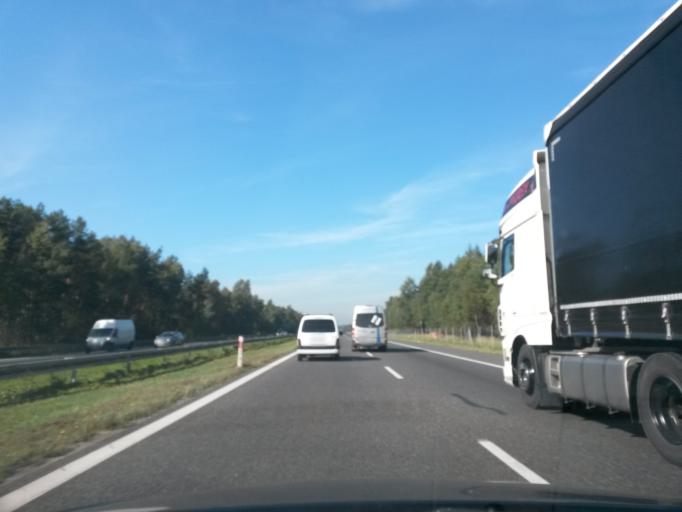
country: PL
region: Lesser Poland Voivodeship
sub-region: Powiat chrzanowski
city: Bolecin
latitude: 50.1144
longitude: 19.5044
